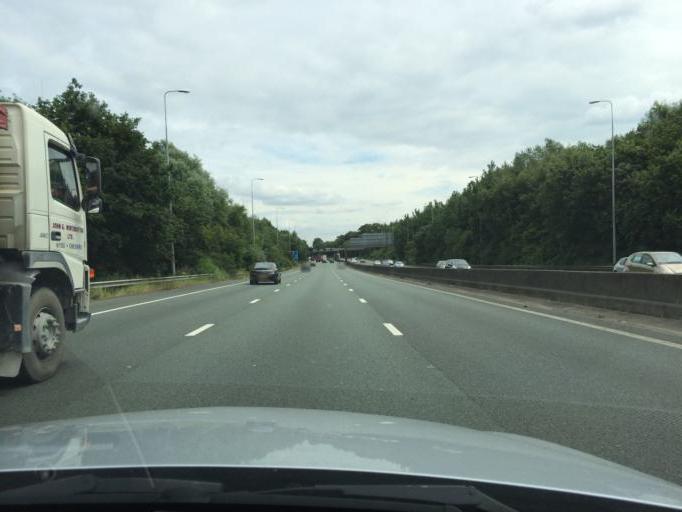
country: GB
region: England
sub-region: Borough of Stockport
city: Cheadle Heath
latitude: 53.4020
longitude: -2.2076
